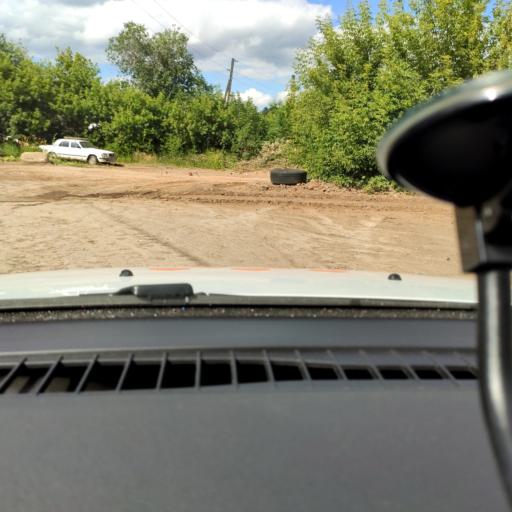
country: RU
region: Samara
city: Samara
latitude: 53.1817
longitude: 50.2196
